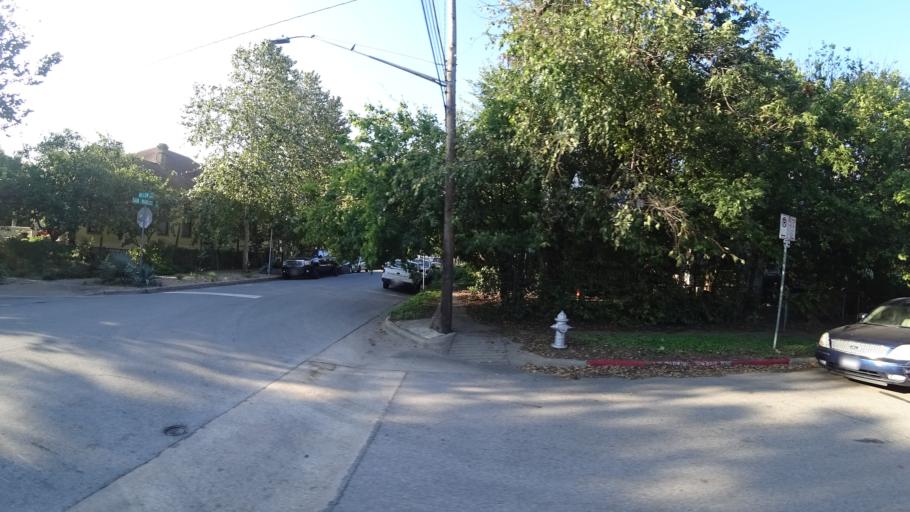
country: US
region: Texas
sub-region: Travis County
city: Austin
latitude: 30.2597
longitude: -97.7351
